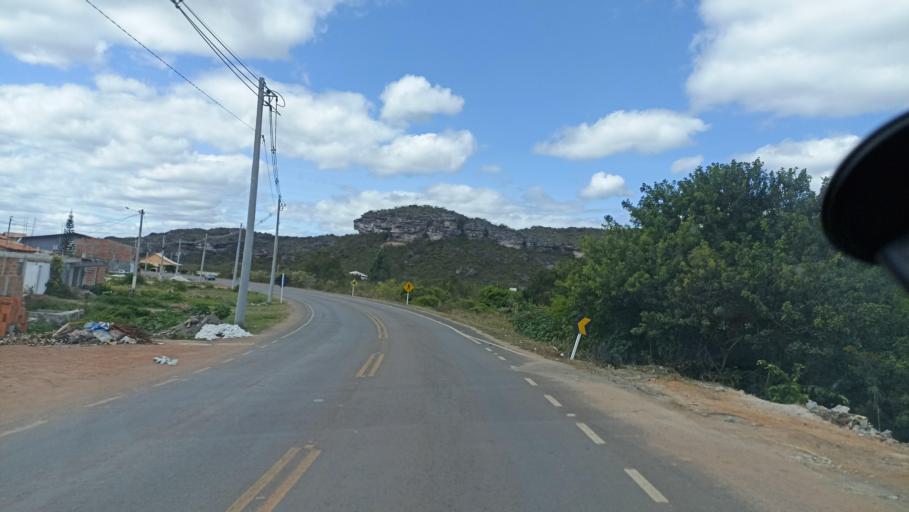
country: BR
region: Bahia
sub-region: Andarai
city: Vera Cruz
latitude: -13.0135
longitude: -41.3712
